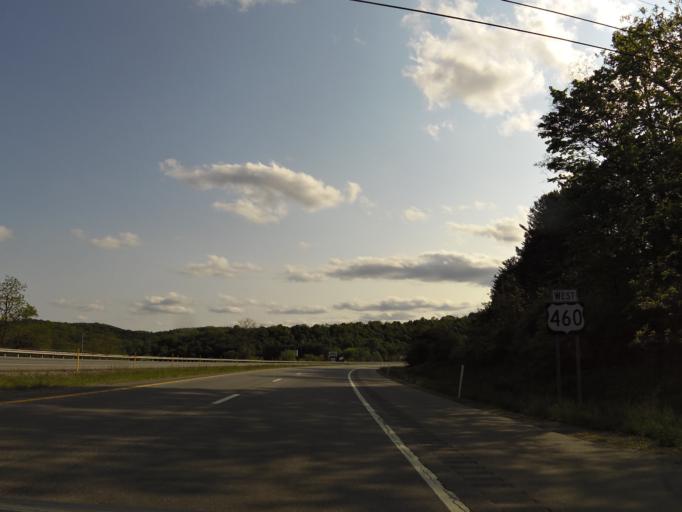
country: US
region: West Virginia
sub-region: Mercer County
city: Princeton
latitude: 37.3481
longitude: -81.1095
